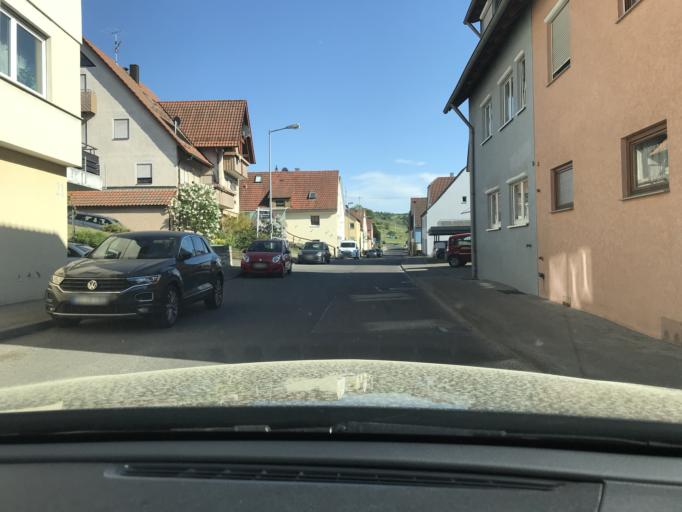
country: DE
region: Baden-Wuerttemberg
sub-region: Regierungsbezirk Stuttgart
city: Weinstadt-Endersbach
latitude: 48.7892
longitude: 9.4054
